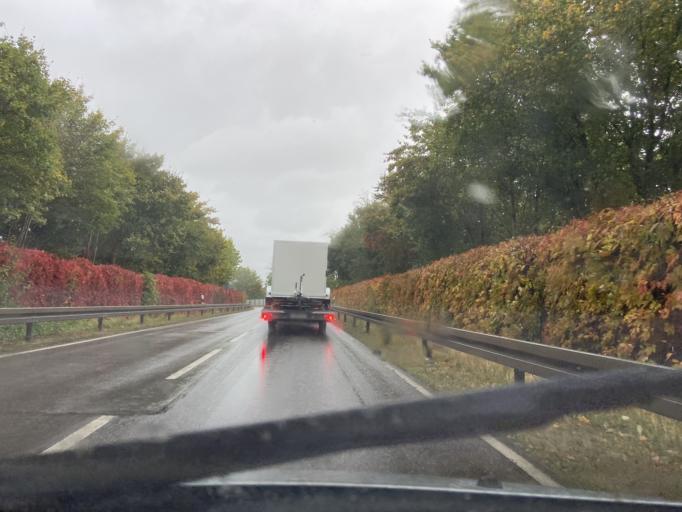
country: DE
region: Baden-Wuerttemberg
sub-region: Tuebingen Region
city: Ennetach
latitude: 48.0504
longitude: 9.3239
